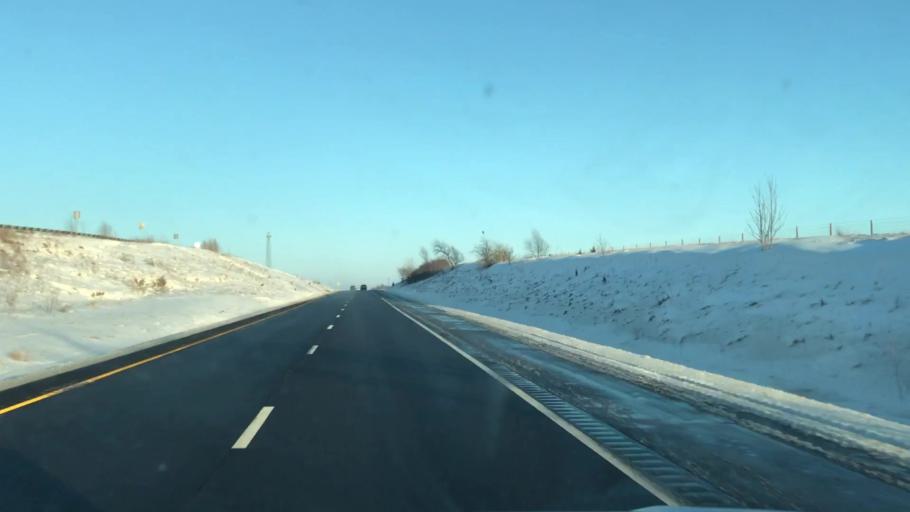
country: US
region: Missouri
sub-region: Clinton County
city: Gower
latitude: 39.7615
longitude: -94.5461
